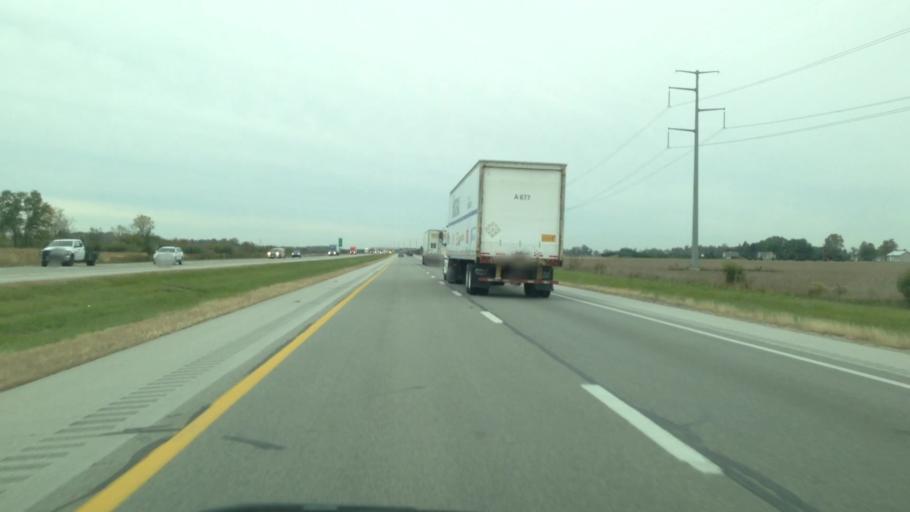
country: US
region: Ohio
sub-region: Fulton County
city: Swanton
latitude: 41.5999
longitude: -83.9240
